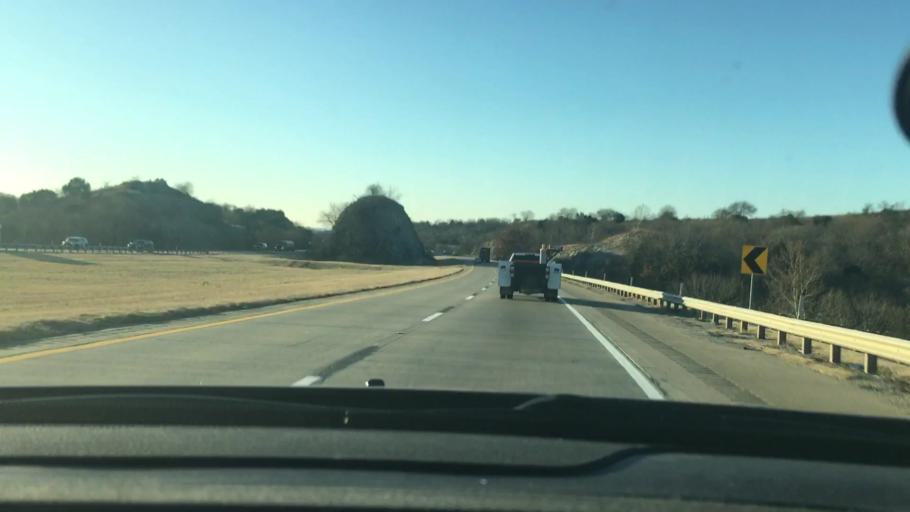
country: US
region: Oklahoma
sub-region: Murray County
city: Davis
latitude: 34.3599
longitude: -97.1487
